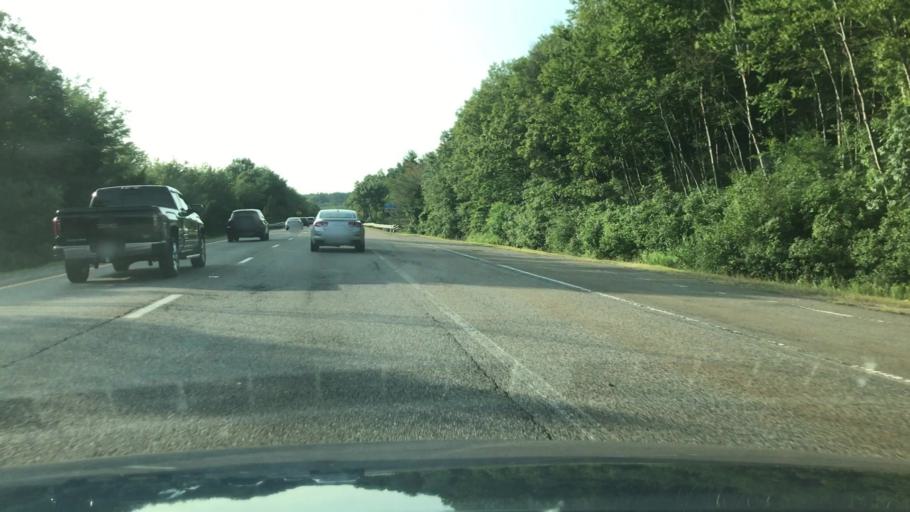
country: US
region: Massachusetts
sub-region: Plymouth County
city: Hanover
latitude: 42.1299
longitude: -70.8065
